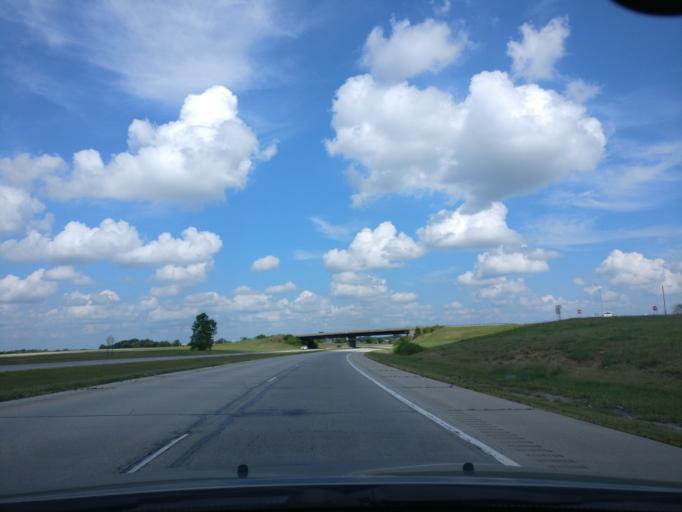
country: US
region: Ohio
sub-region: Greene County
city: Wilberforce
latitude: 39.6893
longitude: -83.8861
